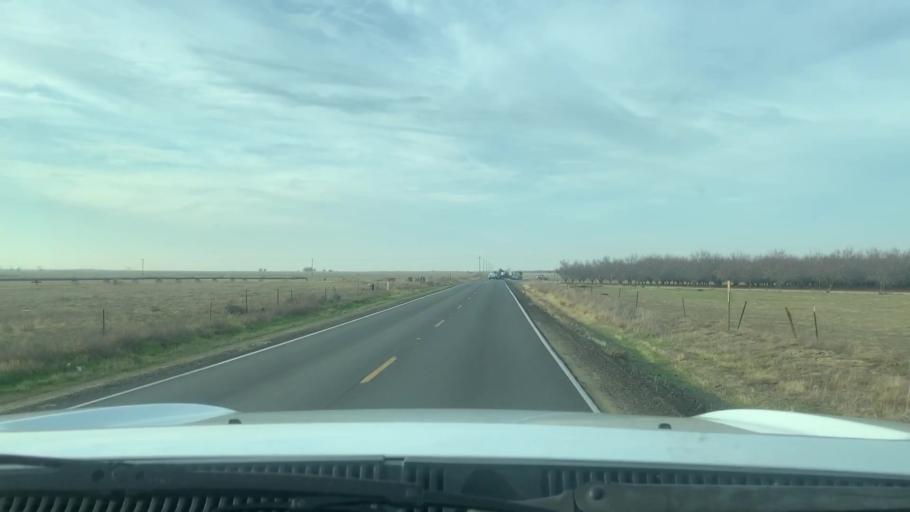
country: US
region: California
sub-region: Kern County
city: Lost Hills
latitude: 35.5563
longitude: -119.7955
